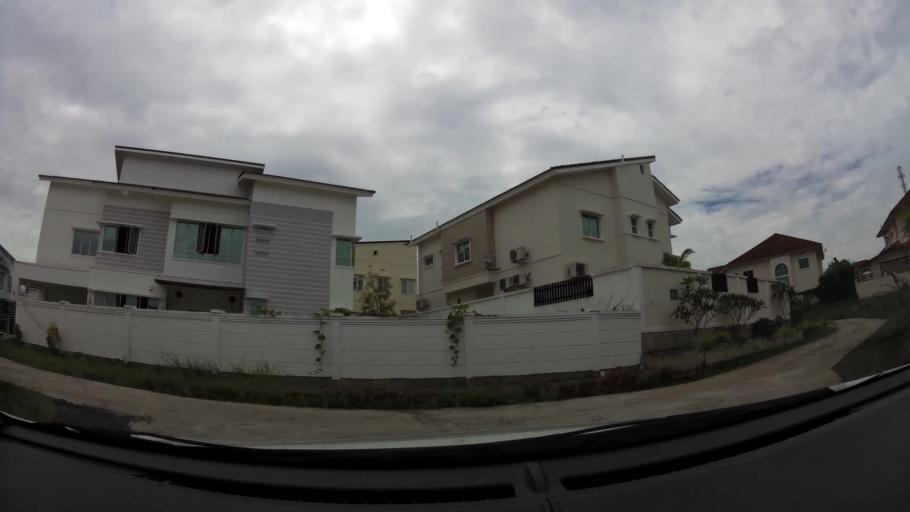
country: BN
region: Brunei and Muara
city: Bandar Seri Begawan
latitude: 4.8889
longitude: 114.9118
